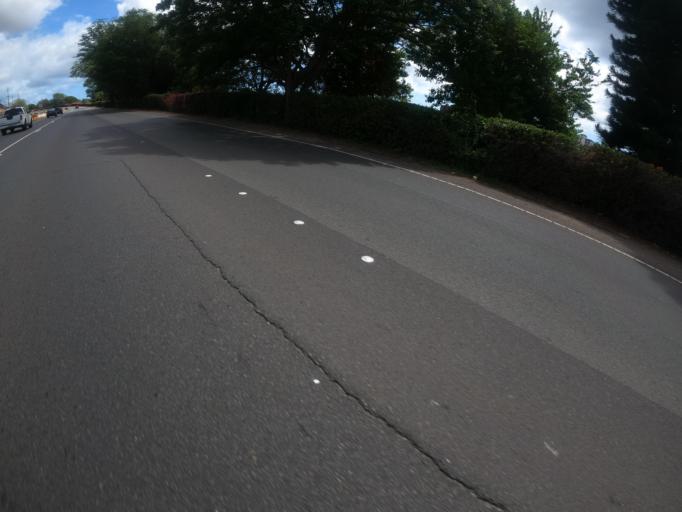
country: US
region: Hawaii
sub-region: Honolulu County
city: Makakilo
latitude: 21.3455
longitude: -158.1224
